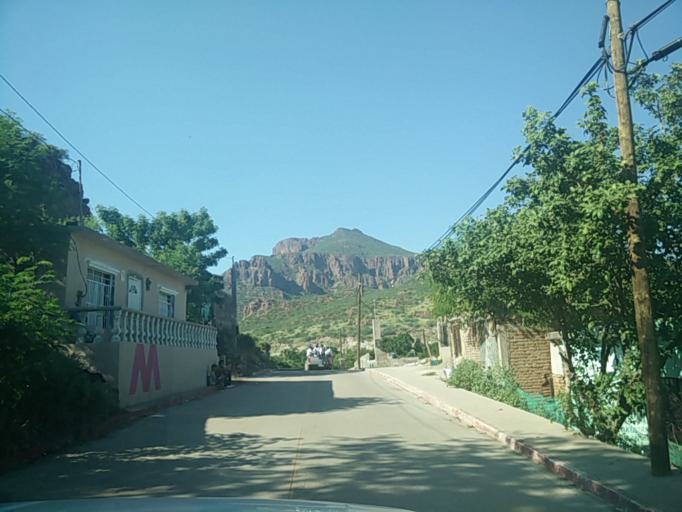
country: MX
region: Sonora
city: Heroica Guaymas
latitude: 27.9371
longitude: -110.8840
